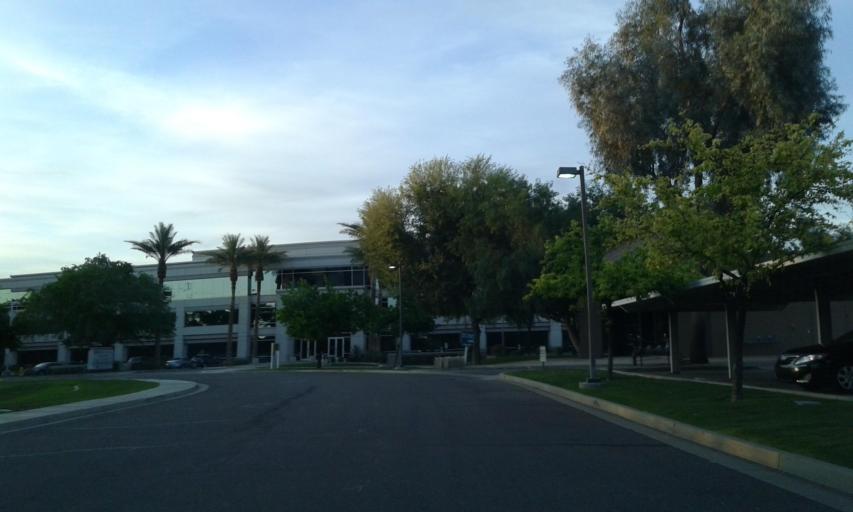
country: US
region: Arizona
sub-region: Maricopa County
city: Glendale
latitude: 33.5845
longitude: -112.1142
